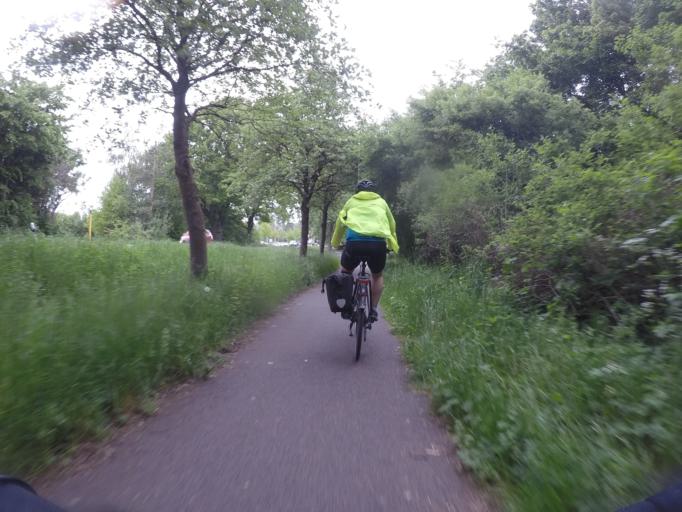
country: DE
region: Schleswig-Holstein
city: Kisdorf
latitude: 53.8002
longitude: 10.0044
